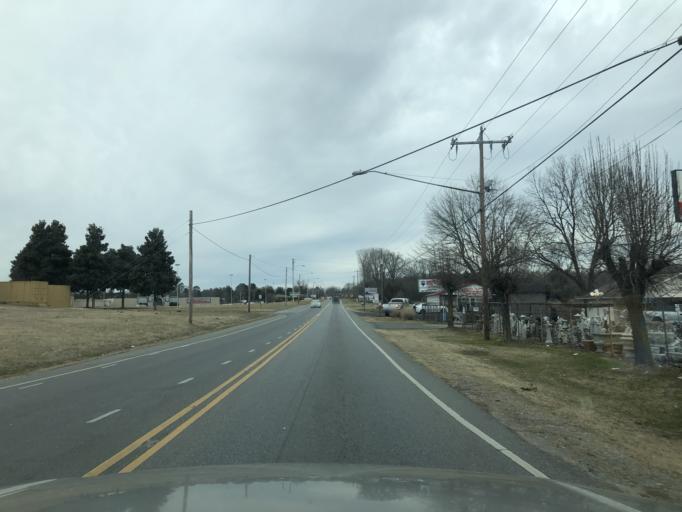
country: US
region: North Carolina
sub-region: Cleveland County
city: Shelby
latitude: 35.2666
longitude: -81.4791
